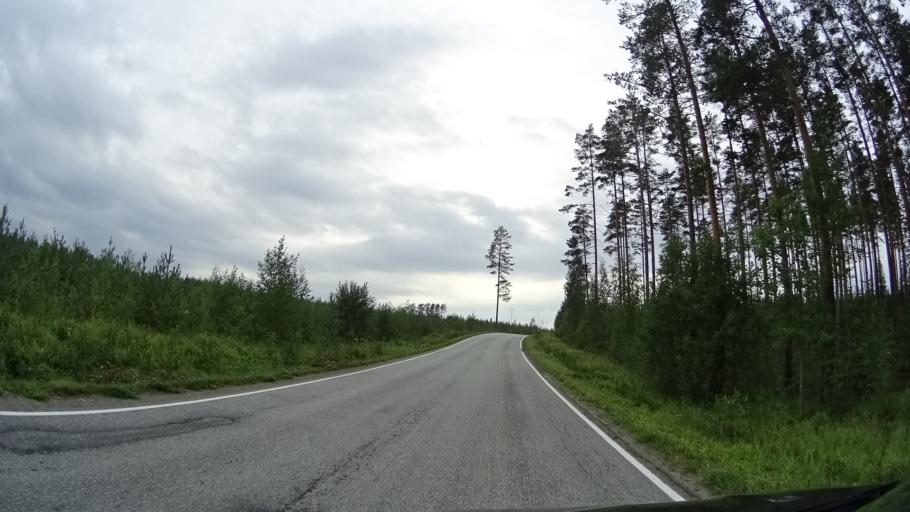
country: FI
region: Southern Savonia
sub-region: Savonlinna
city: Punkaharju
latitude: 61.7497
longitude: 29.4751
